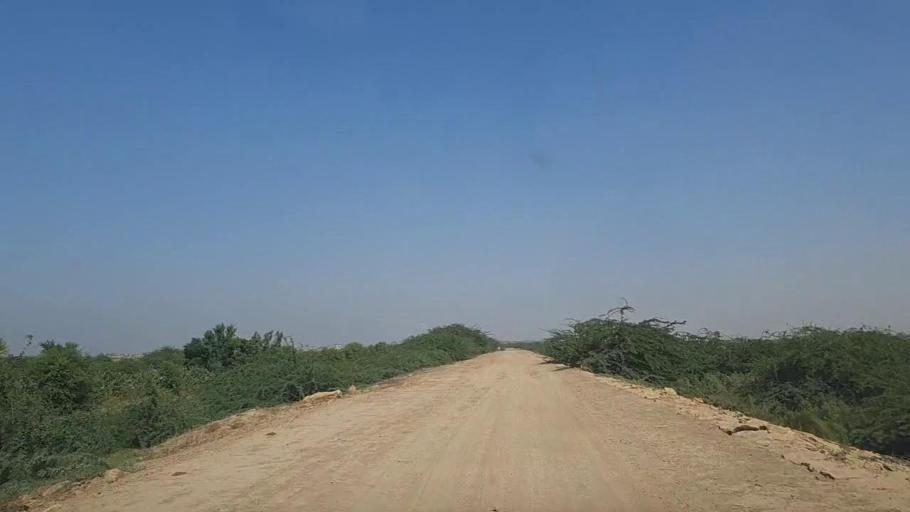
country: PK
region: Sindh
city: Daro Mehar
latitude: 24.8816
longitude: 68.0561
